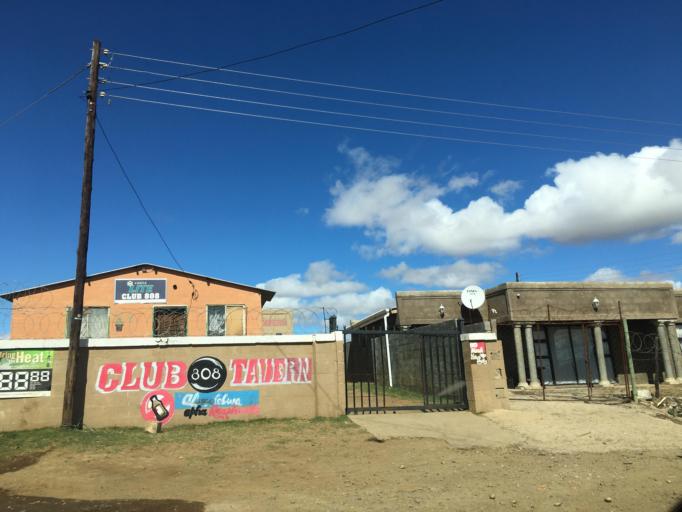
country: ZA
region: Eastern Cape
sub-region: Chris Hani District Municipality
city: Cala
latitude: -31.5439
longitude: 27.6847
